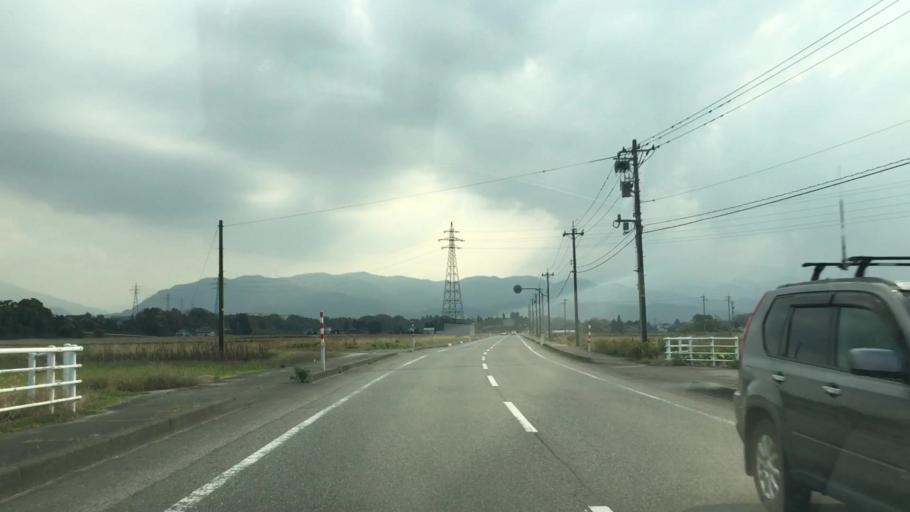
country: JP
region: Toyama
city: Yatsuomachi-higashikumisaka
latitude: 36.6093
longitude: 137.1924
